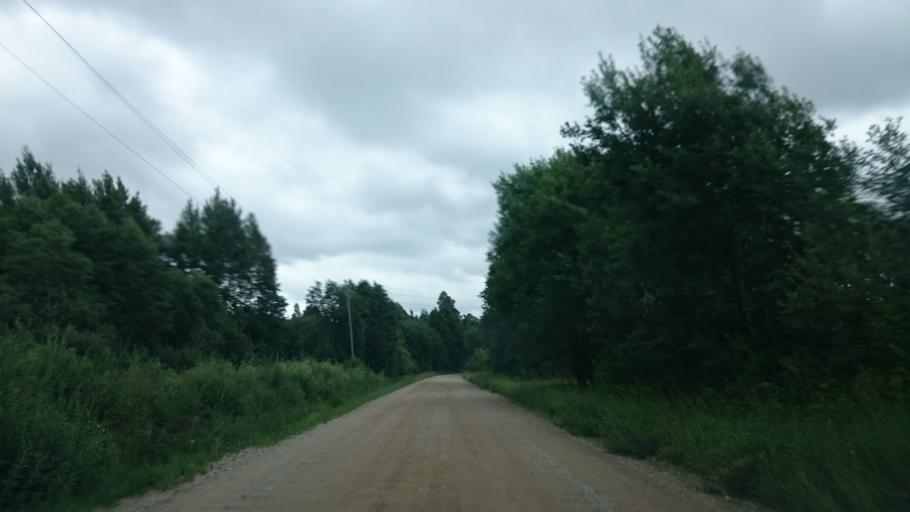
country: LV
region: Durbe
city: Liegi
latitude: 56.7529
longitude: 21.3541
